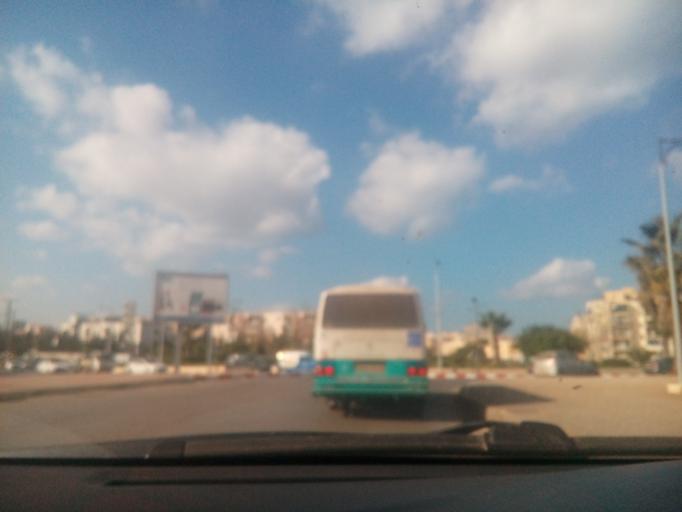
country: DZ
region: Oran
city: Oran
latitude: 35.7021
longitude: -0.5972
